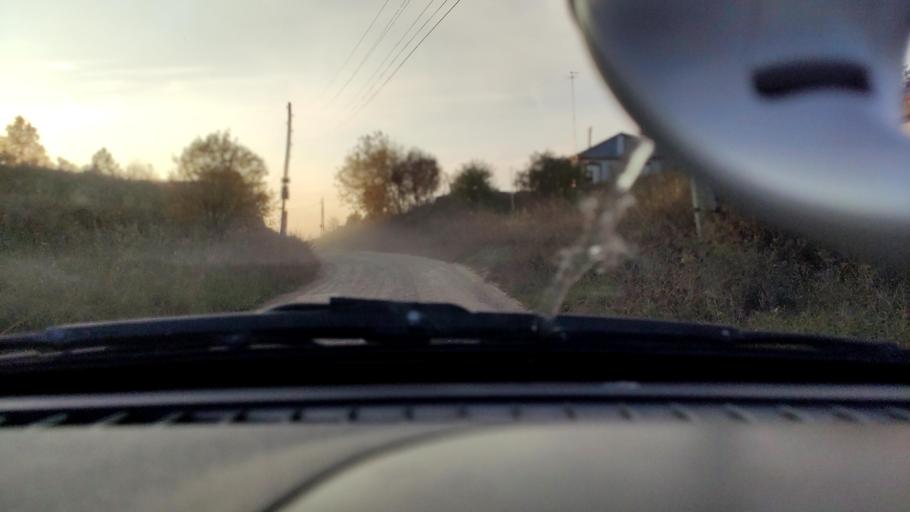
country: RU
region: Perm
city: Lobanovo
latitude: 57.8516
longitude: 56.3400
